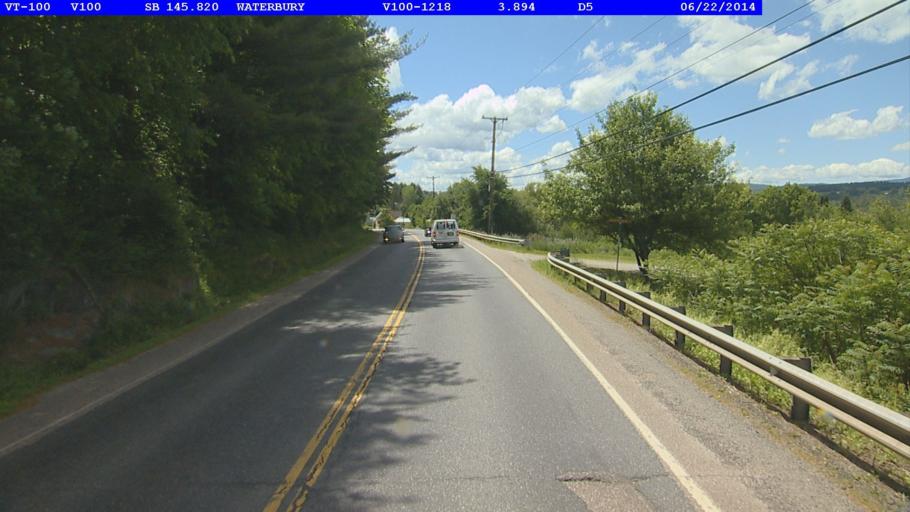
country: US
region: Vermont
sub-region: Washington County
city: Waterbury
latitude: 44.3852
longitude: -72.7205
